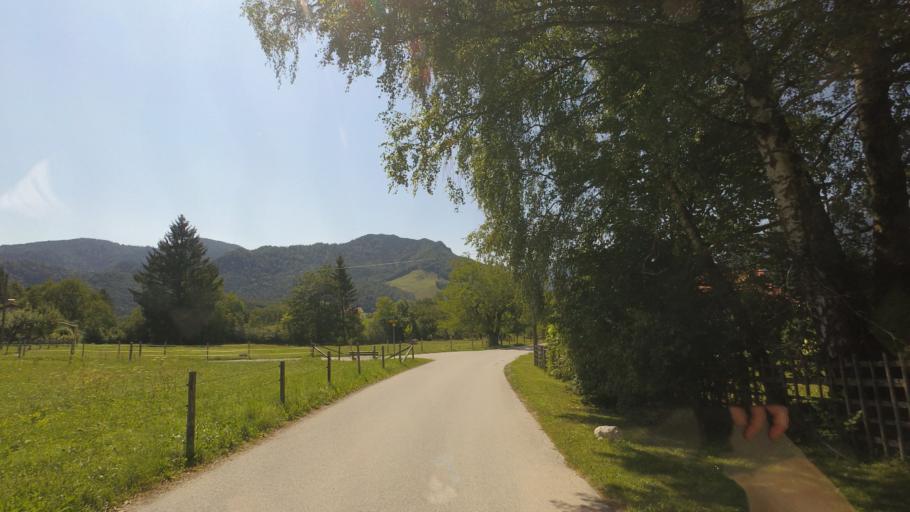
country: DE
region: Bavaria
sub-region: Upper Bavaria
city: Unterwossen
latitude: 47.7351
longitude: 12.4718
